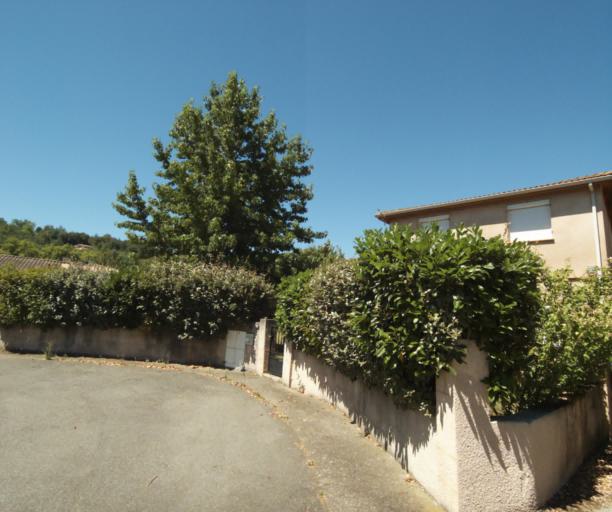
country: FR
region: Midi-Pyrenees
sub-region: Departement de la Haute-Garonne
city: Pechabou
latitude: 43.5094
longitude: 1.5075
